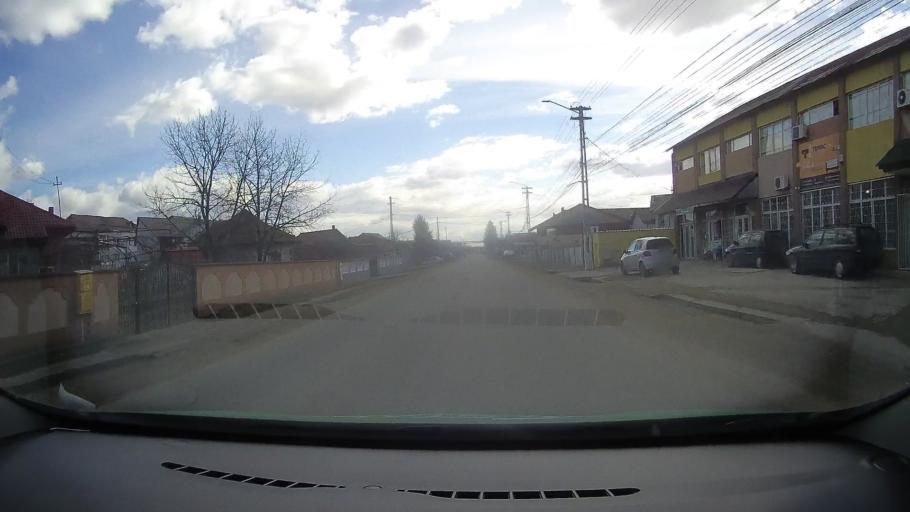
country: RO
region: Dambovita
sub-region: Comuna Doicesti
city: Doicesti
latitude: 44.9835
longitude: 25.3876
